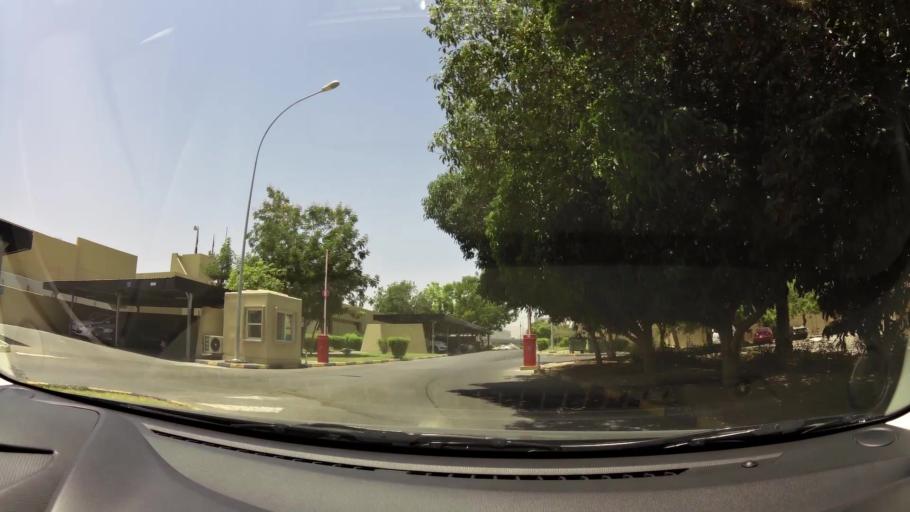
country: OM
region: Muhafazat Masqat
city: Bawshar
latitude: 23.5999
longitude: 58.4435
